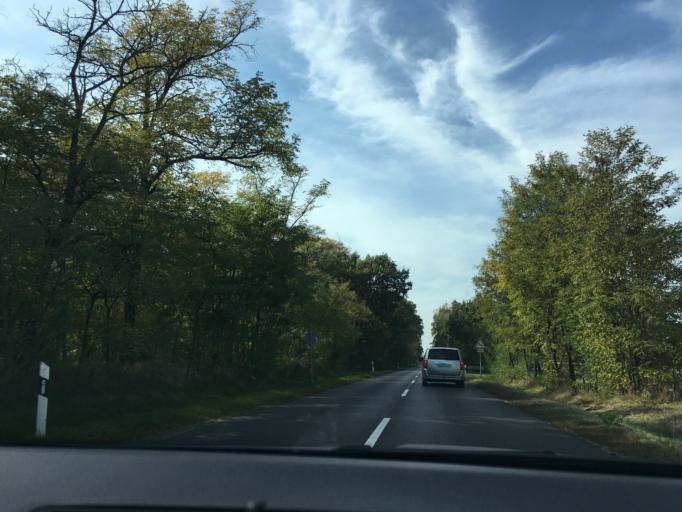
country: HU
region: Hajdu-Bihar
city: Vamospercs
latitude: 47.5277
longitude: 21.8542
